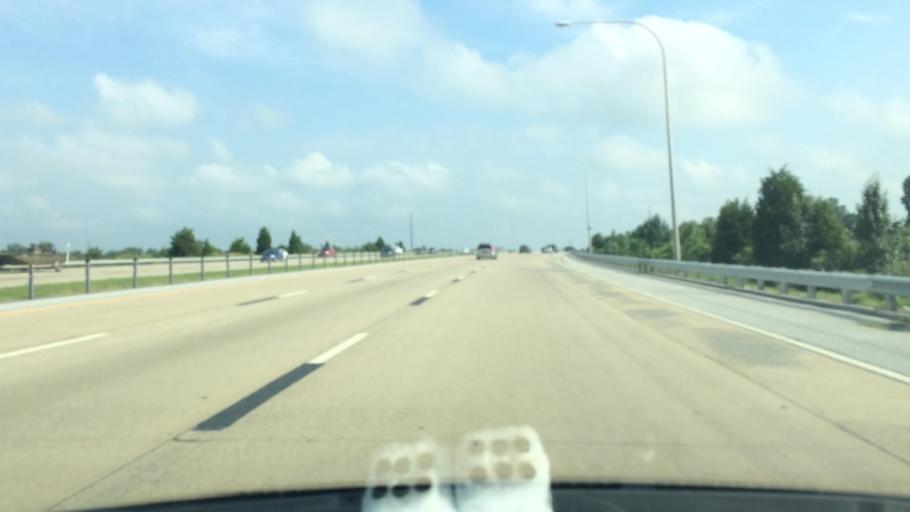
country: US
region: Delaware
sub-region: New Castle County
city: Bear
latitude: 39.5865
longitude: -75.6616
